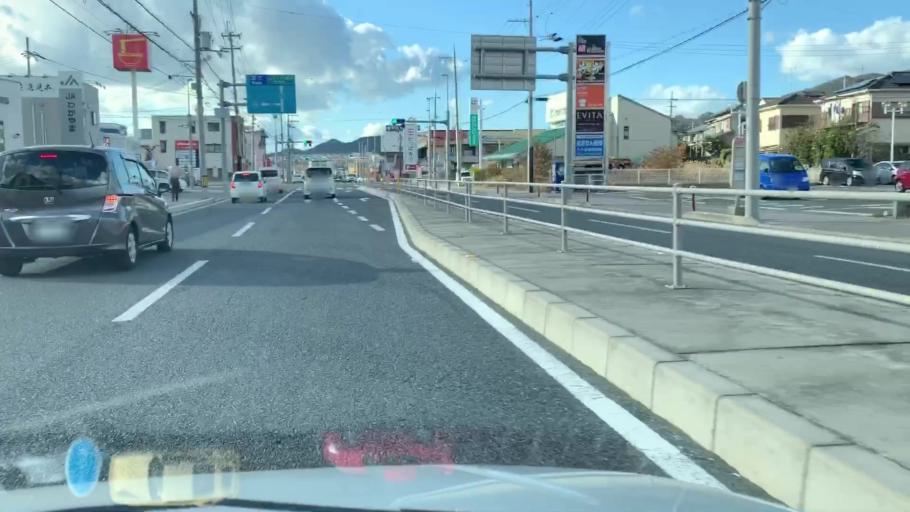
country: JP
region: Wakayama
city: Wakayama-shi
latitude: 34.2621
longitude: 135.2016
